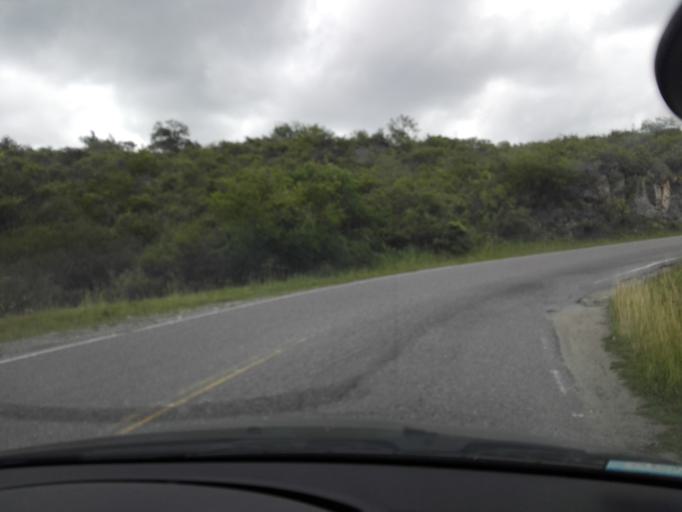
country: AR
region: Cordoba
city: Alta Gracia
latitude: -31.5904
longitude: -64.5039
